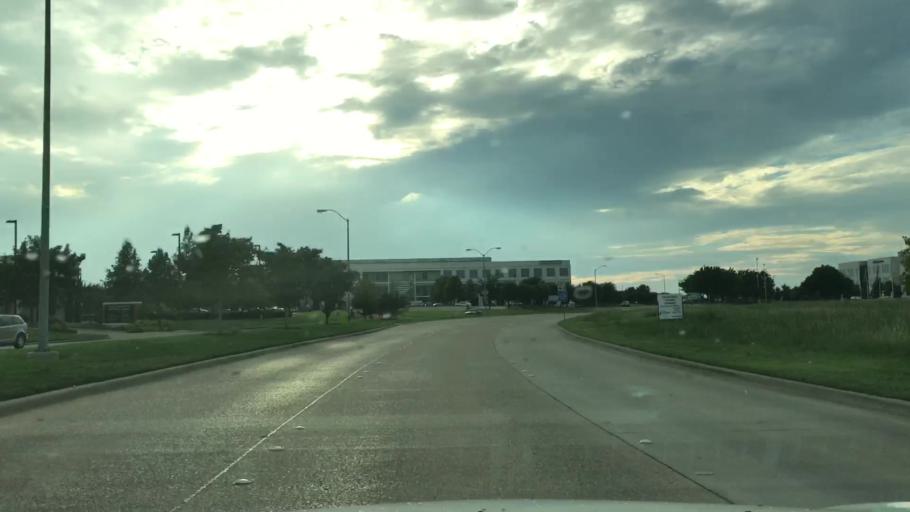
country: US
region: Texas
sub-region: Dallas County
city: Addison
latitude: 33.0164
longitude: -96.8303
